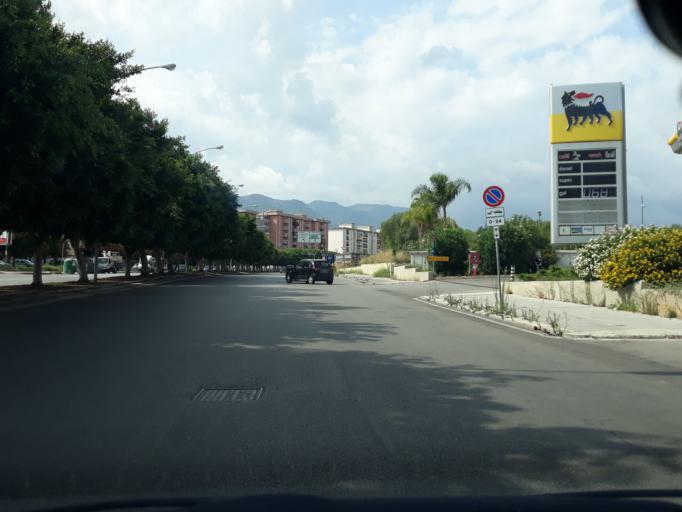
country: IT
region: Sicily
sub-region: Palermo
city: Palermo
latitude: 38.1000
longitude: 13.3469
